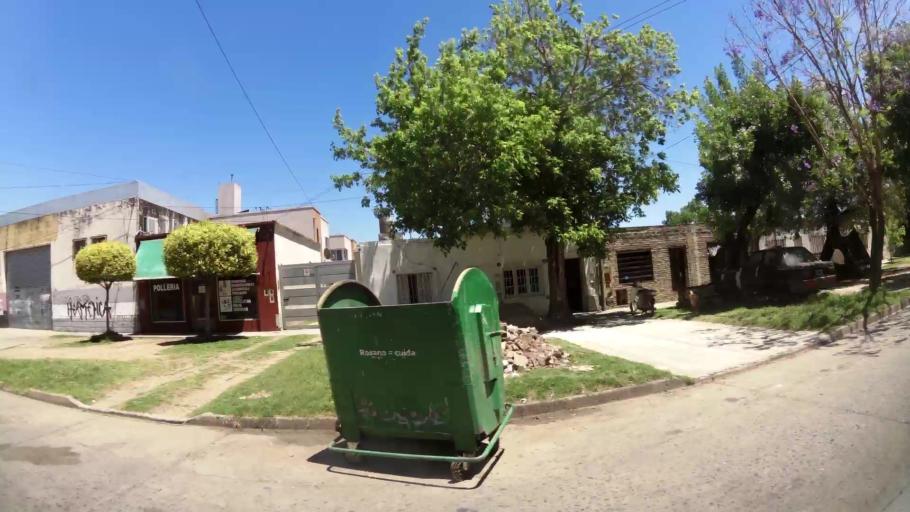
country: AR
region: Santa Fe
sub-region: Departamento de Rosario
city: Rosario
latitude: -32.9491
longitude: -60.7019
